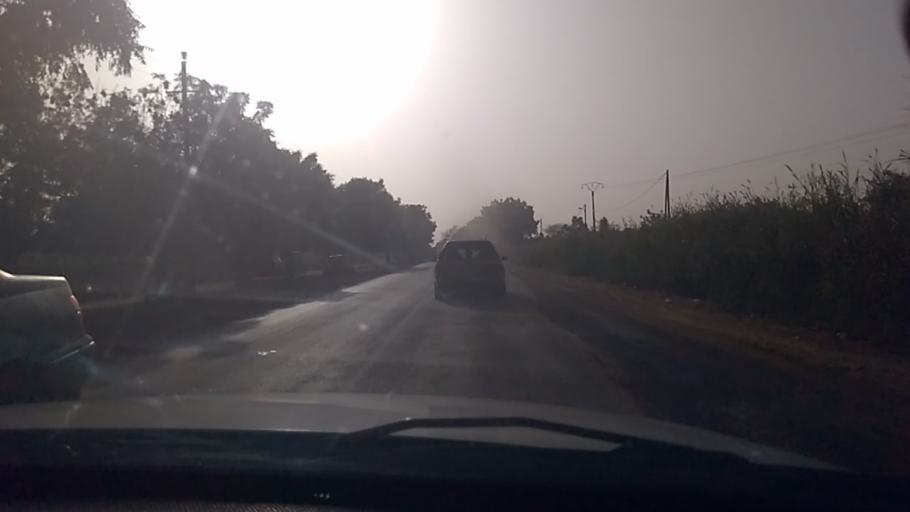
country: SN
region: Thies
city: Khombole
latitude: 14.7627
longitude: -16.8159
